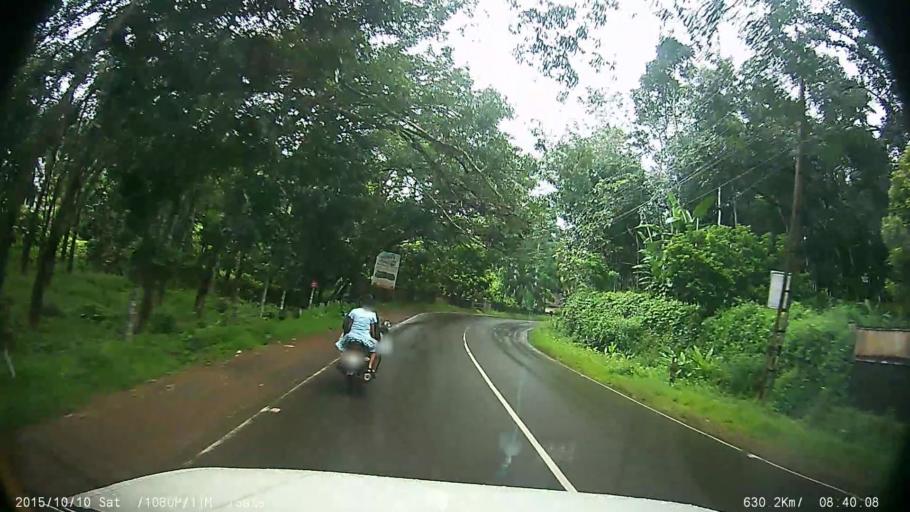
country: IN
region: Kerala
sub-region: Kottayam
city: Palackattumala
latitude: 9.7573
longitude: 76.5528
